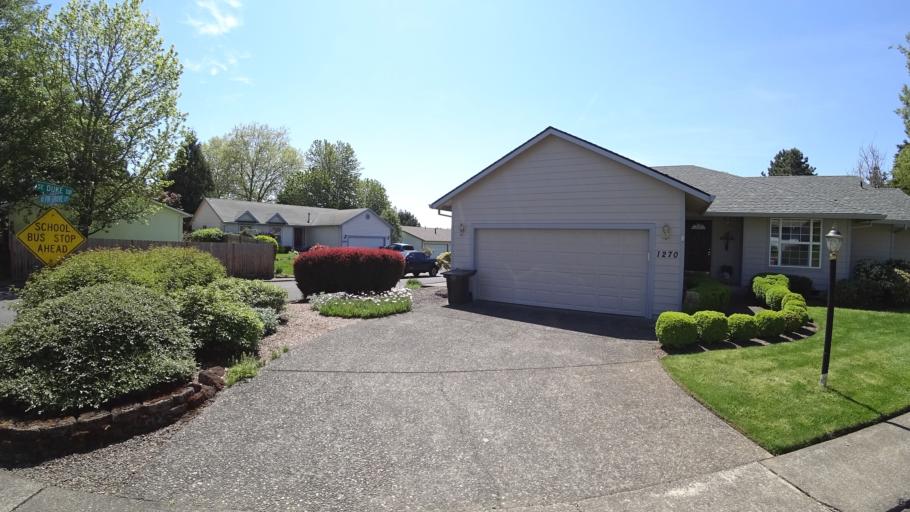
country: US
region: Oregon
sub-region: Washington County
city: Hillsboro
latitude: 45.5067
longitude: -122.9711
